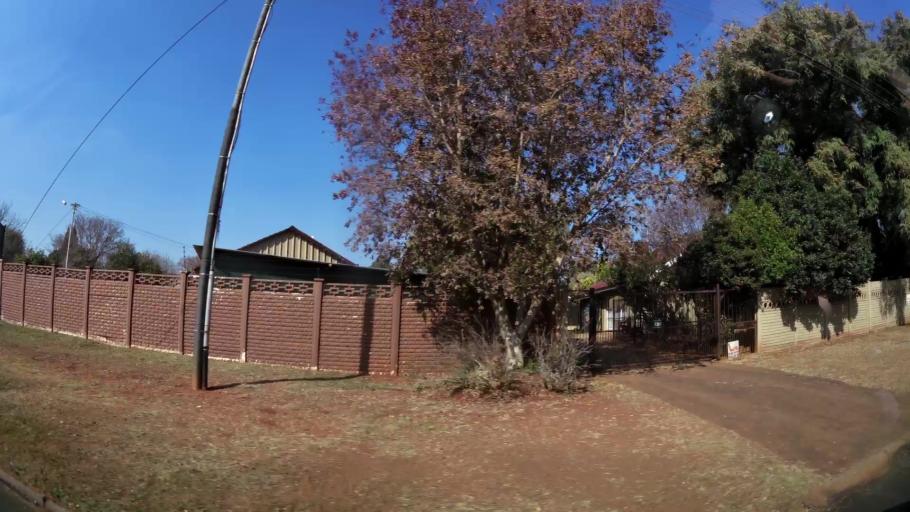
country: ZA
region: Gauteng
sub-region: West Rand District Municipality
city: Randfontein
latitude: -26.1648
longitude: 27.6895
